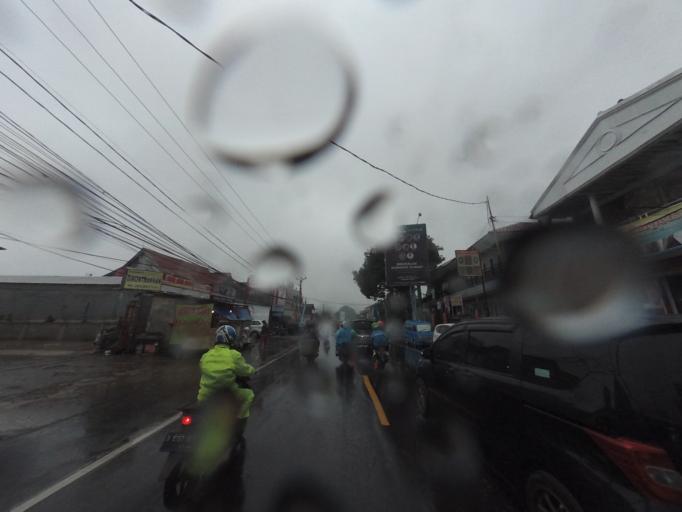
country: ID
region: West Java
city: Caringin
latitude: -6.6549
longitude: 106.8616
